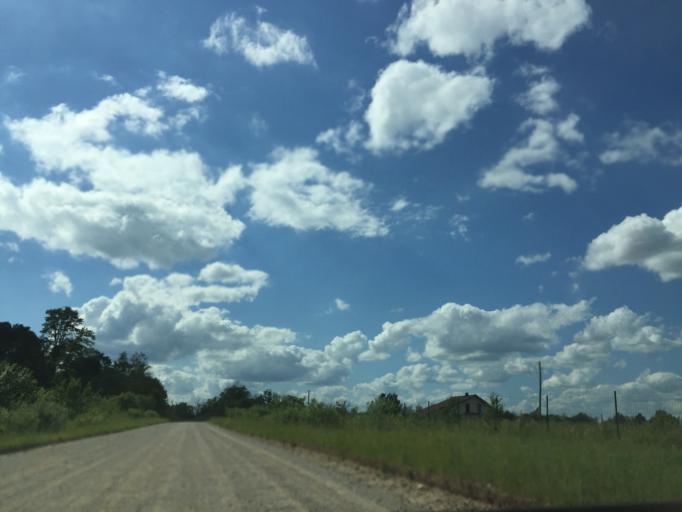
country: LV
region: Tukuma Rajons
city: Tukums
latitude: 56.9043
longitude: 23.1440
